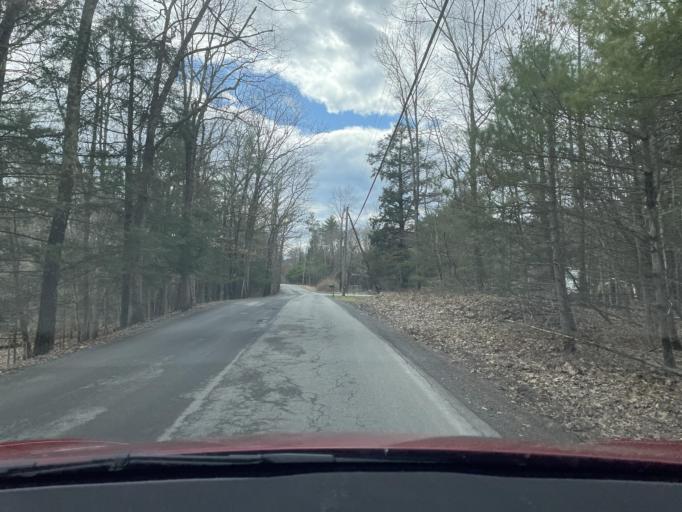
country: US
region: New York
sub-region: Ulster County
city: Zena
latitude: 42.0401
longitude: -74.0525
